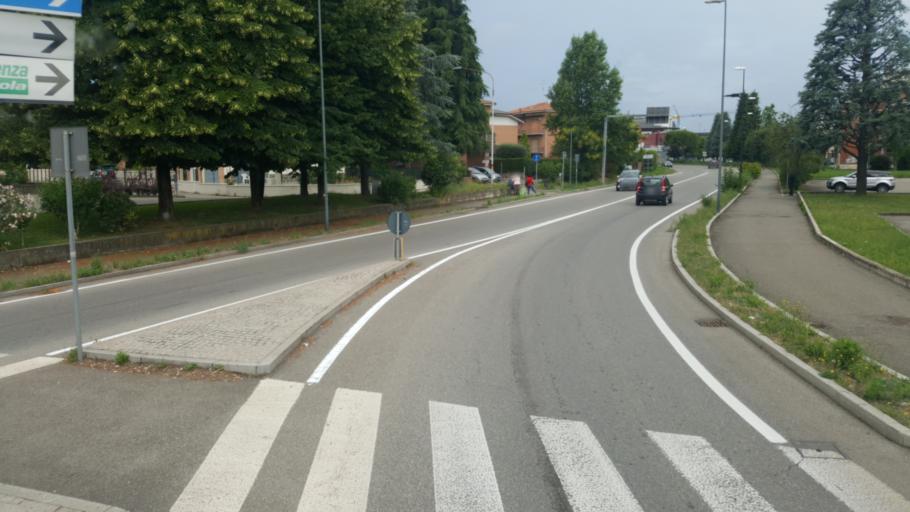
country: IT
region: Emilia-Romagna
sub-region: Provincia di Modena
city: Vignola
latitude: 44.4915
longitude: 11.0160
